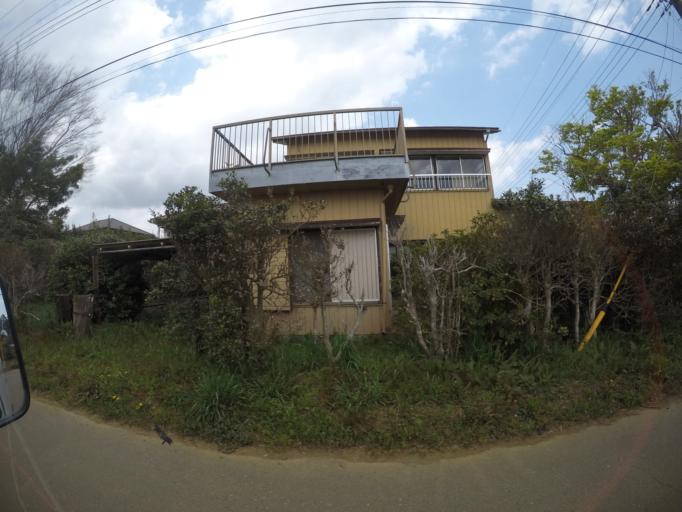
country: JP
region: Chiba
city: Sawara
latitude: 35.8295
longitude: 140.5229
